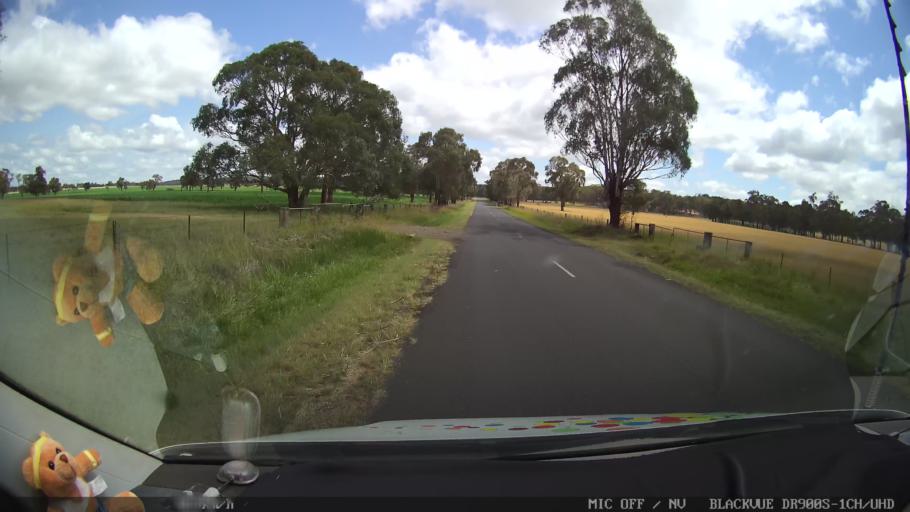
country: AU
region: New South Wales
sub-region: Glen Innes Severn
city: Glen Innes
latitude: -29.6059
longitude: 151.6669
